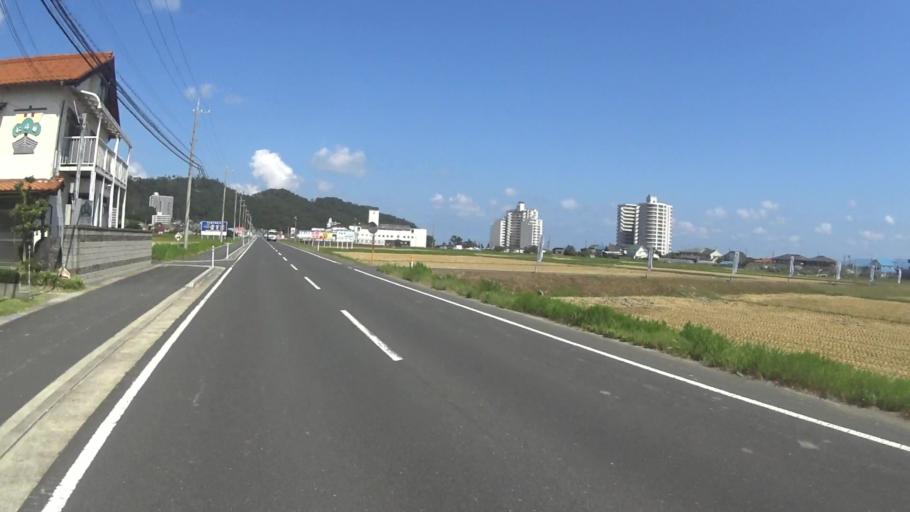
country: JP
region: Kyoto
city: Miyazu
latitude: 35.6105
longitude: 135.2276
